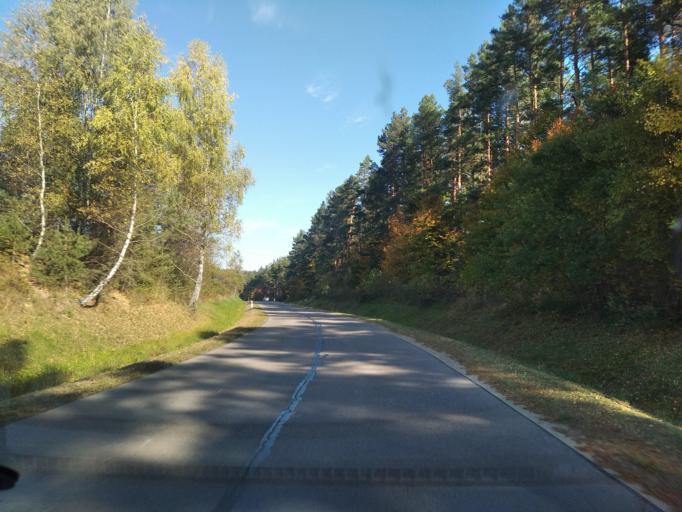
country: PL
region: Subcarpathian Voivodeship
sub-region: Powiat sanocki
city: Bukowsko
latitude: 49.4136
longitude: 21.9524
